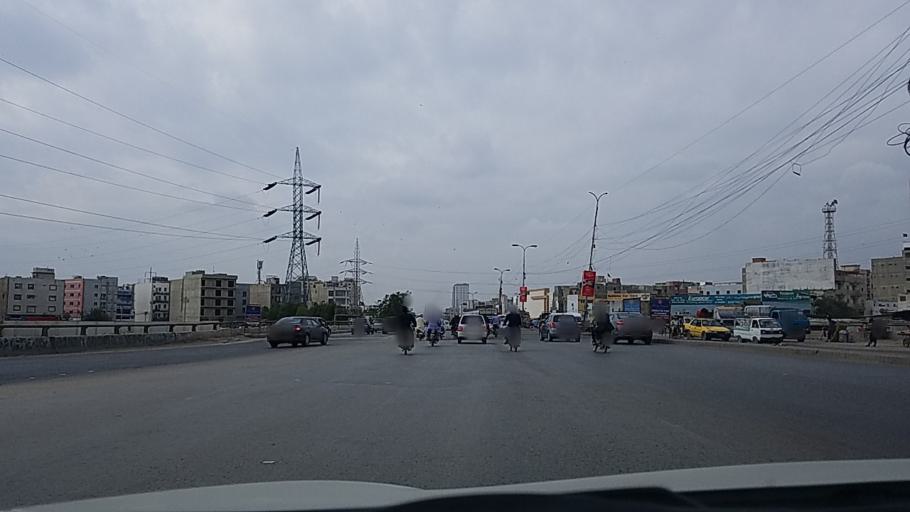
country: PK
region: Sindh
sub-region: Karachi District
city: Karachi
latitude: 24.8319
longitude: 67.0769
